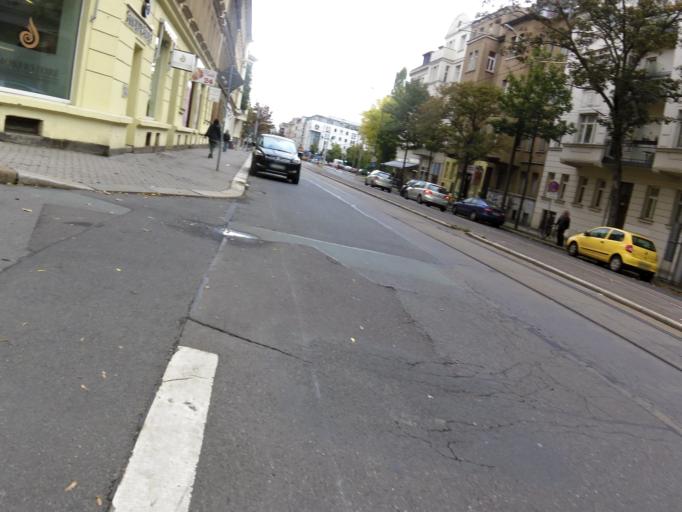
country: DE
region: Saxony
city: Leipzig
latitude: 51.3296
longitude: 12.4045
